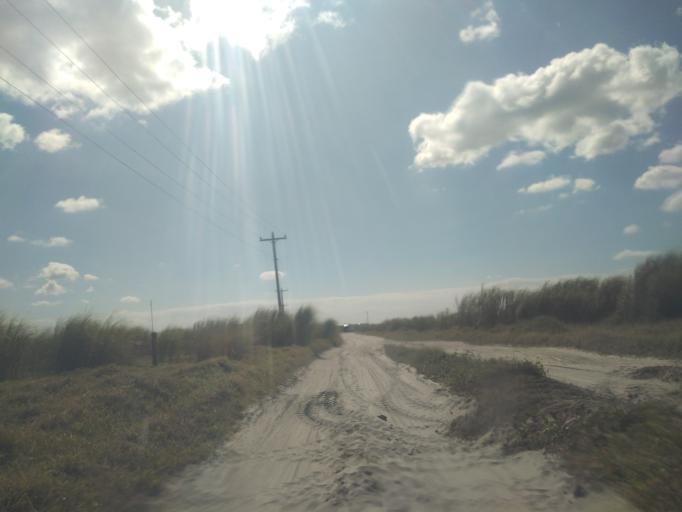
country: PH
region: Central Luzon
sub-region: Province of Pampanga
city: Balas
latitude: 15.0622
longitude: 120.5942
